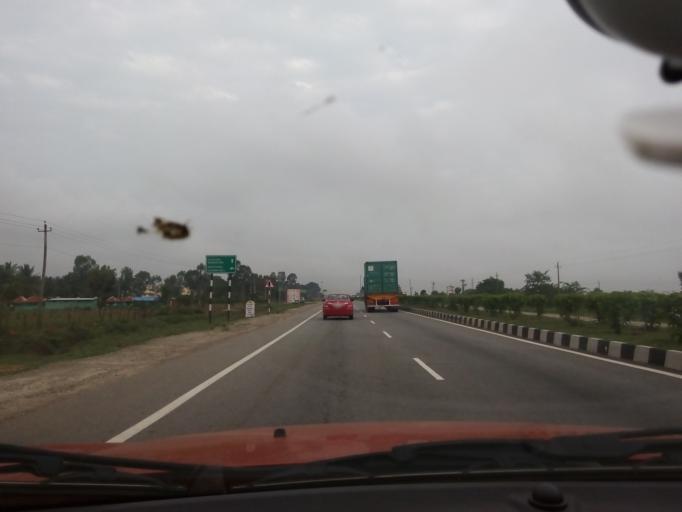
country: IN
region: Karnataka
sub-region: Mandya
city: Belluru
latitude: 12.9626
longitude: 76.6467
